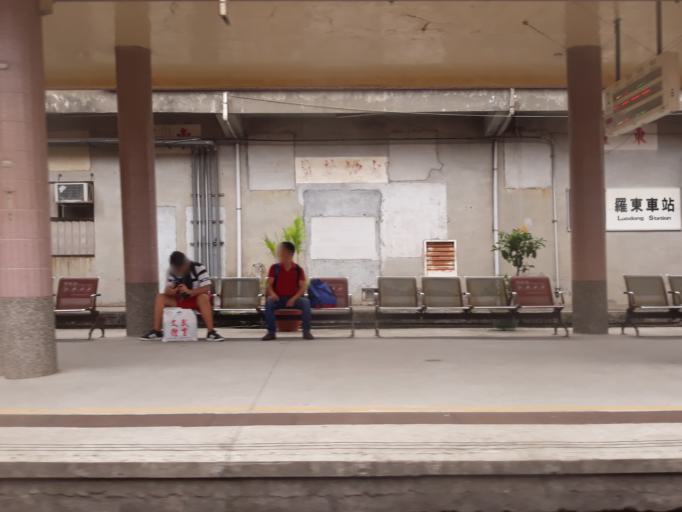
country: TW
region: Taiwan
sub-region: Yilan
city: Yilan
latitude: 24.6784
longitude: 121.7745
